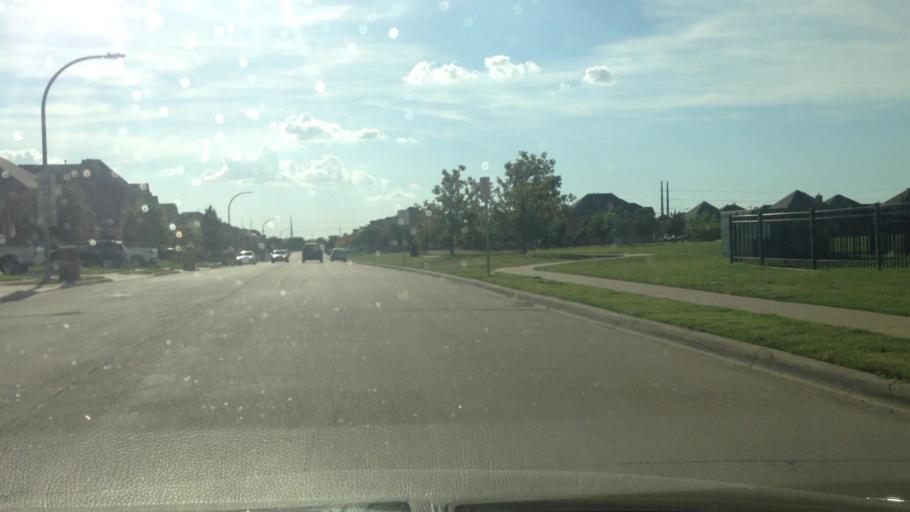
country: US
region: Texas
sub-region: Tarrant County
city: Haslet
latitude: 32.9375
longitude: -97.3875
